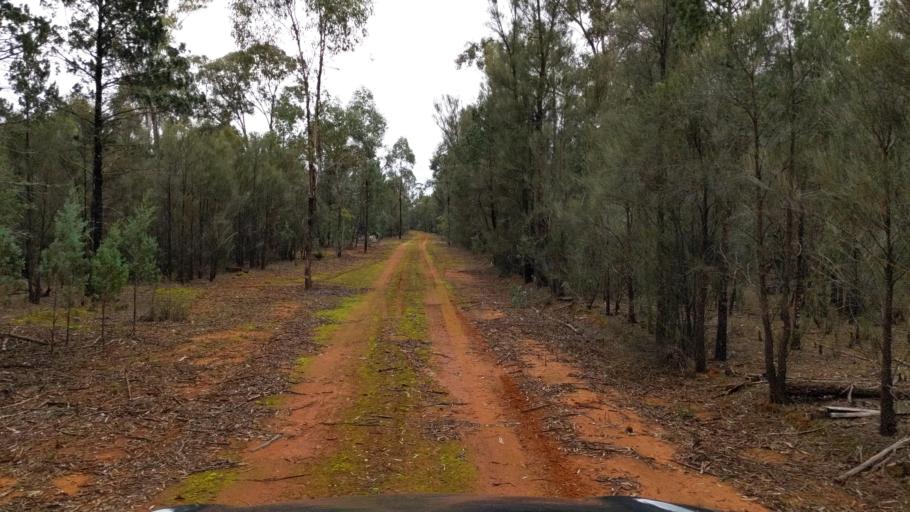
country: AU
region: New South Wales
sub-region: Coolamon
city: Coolamon
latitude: -34.8345
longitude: 146.9348
